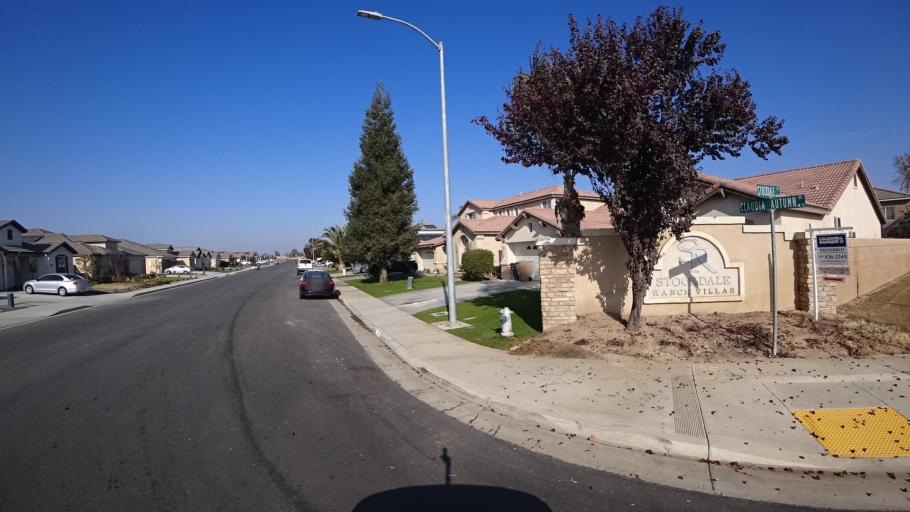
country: US
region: California
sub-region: Kern County
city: Rosedale
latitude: 35.3546
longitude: -119.1676
